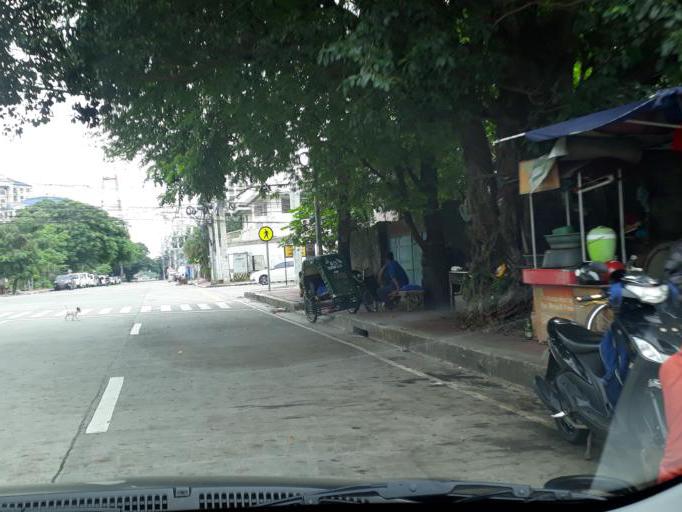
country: PH
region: Metro Manila
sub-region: Quezon City
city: Quezon City
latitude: 14.6356
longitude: 121.0403
